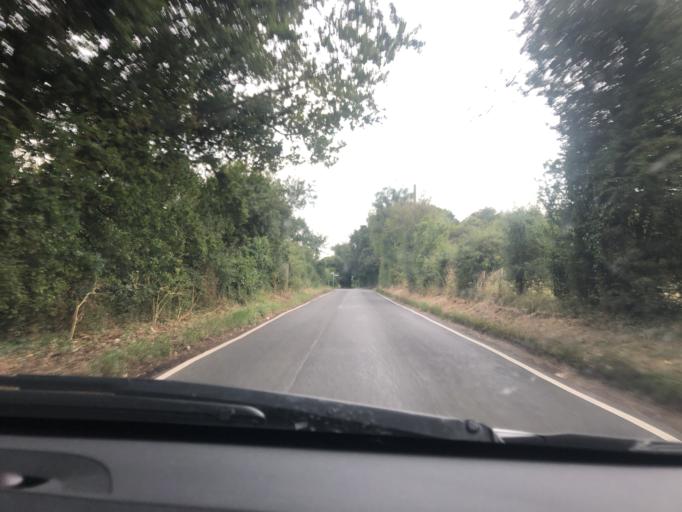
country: GB
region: England
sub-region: Kent
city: Sturry
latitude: 51.3105
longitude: 1.1365
